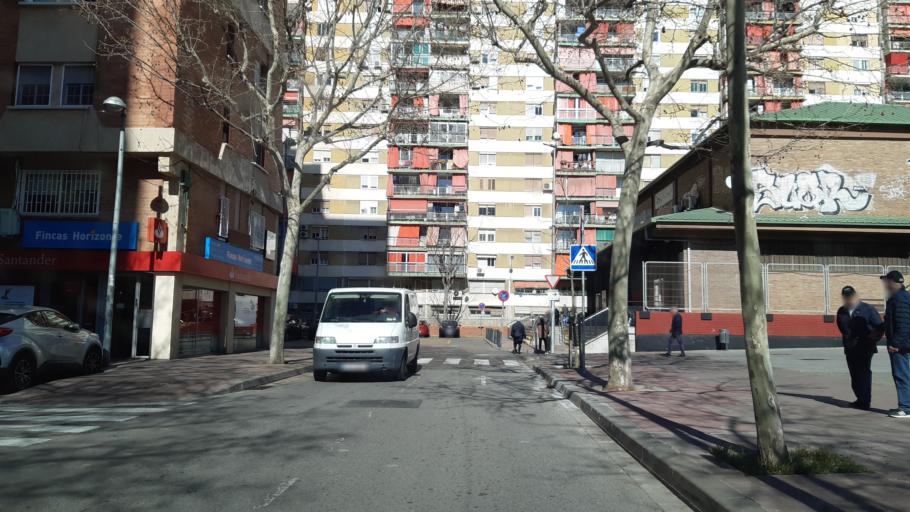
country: ES
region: Catalonia
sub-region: Provincia de Barcelona
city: L'Hospitalet de Llobregat
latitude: 41.3524
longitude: 2.1123
